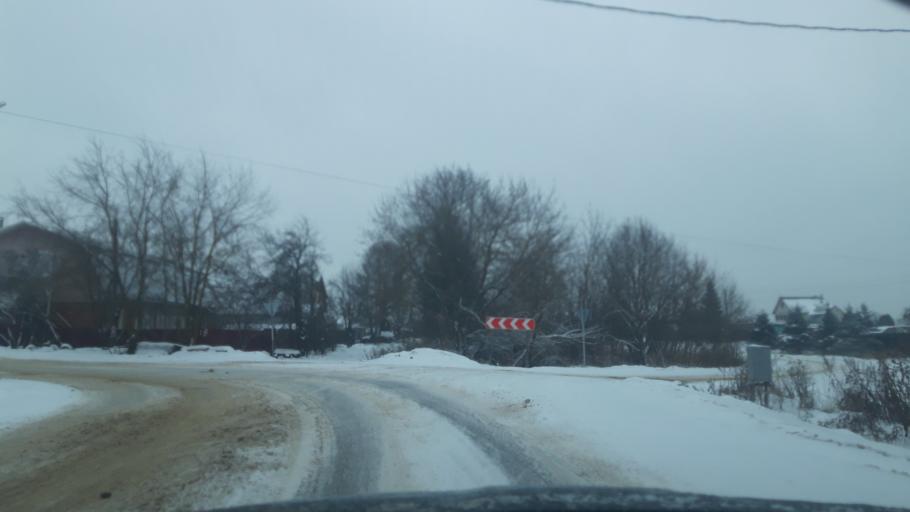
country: RU
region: Moskovskaya
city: Yakhroma
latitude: 56.2931
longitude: 37.4647
